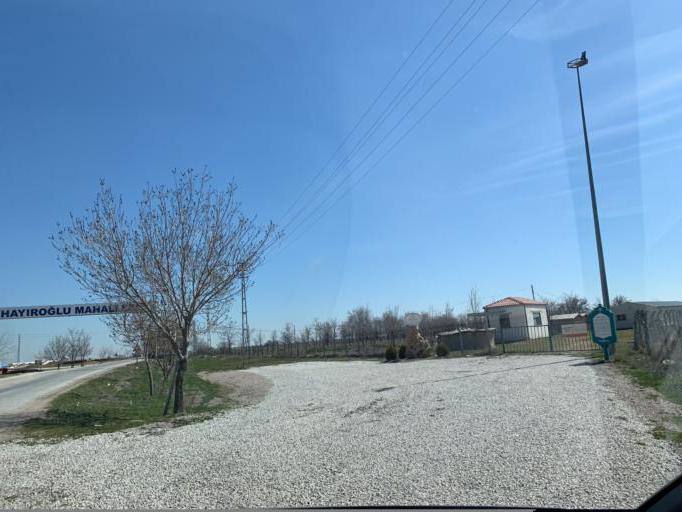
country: TR
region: Konya
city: Yarma
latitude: 37.7524
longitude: 32.8652
